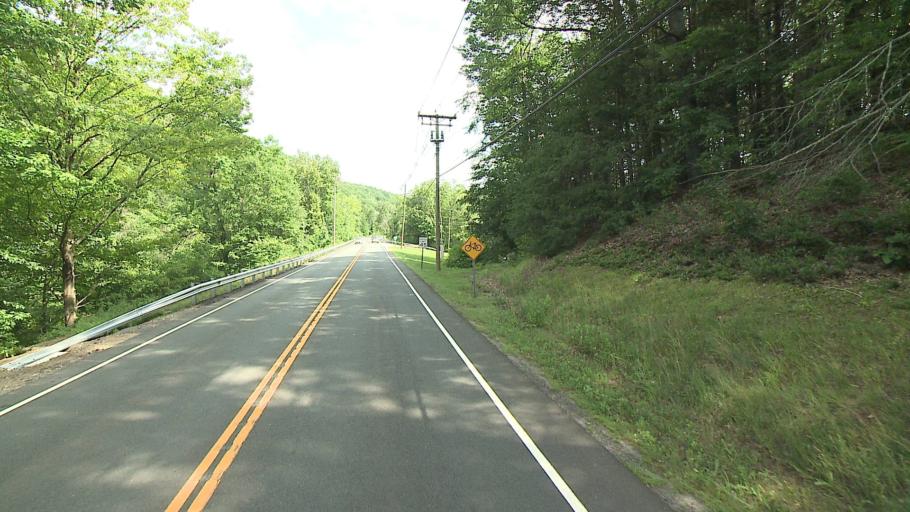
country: US
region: Connecticut
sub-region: Litchfield County
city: Winsted
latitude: 41.8895
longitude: -73.0744
